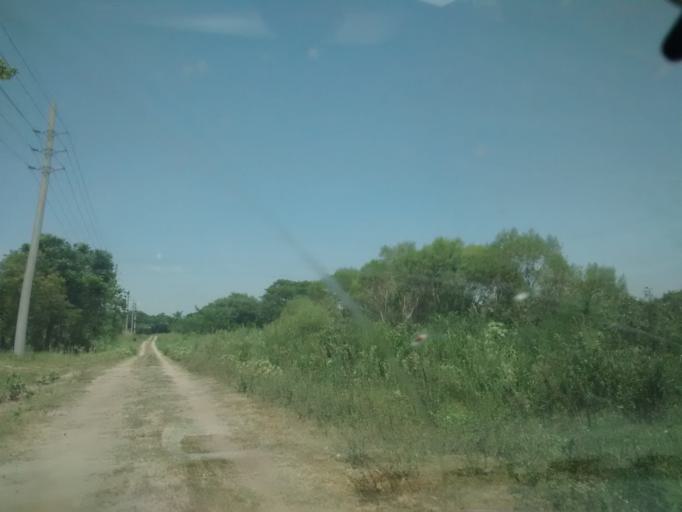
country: AR
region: Chaco
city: Fontana
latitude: -27.4211
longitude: -58.9871
